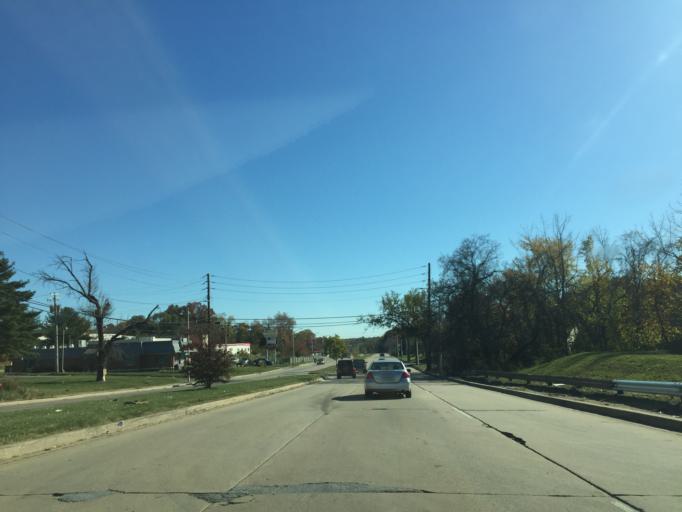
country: US
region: Maryland
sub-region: Baltimore County
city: Baltimore Highlands
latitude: 39.2475
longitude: -76.6377
